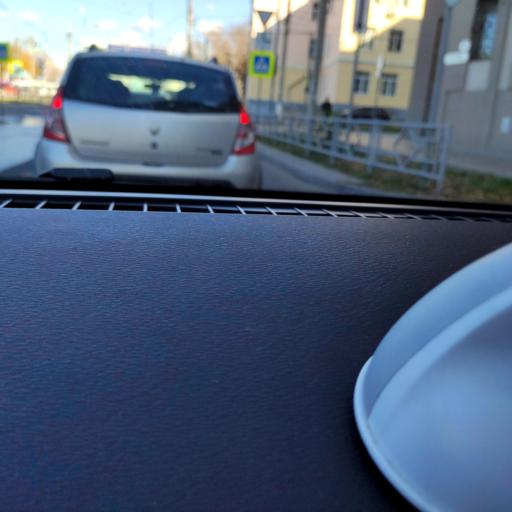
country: RU
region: Samara
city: Rozhdestveno
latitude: 53.1828
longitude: 50.0759
